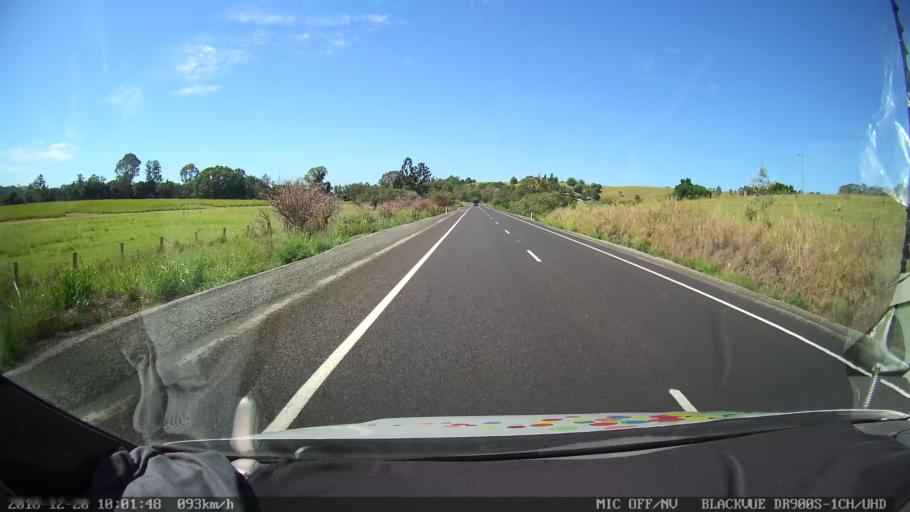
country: AU
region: New South Wales
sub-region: Lismore Municipality
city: Lismore
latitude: -28.8495
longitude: 153.2614
